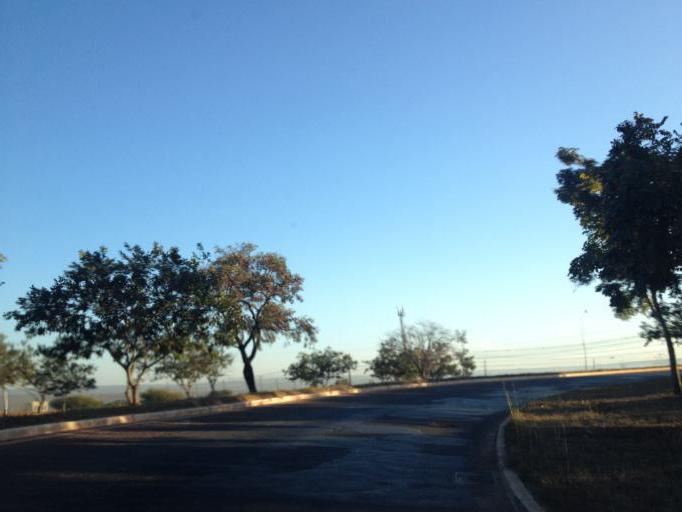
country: BR
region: Federal District
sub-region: Brasilia
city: Brasilia
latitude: -15.7568
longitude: -47.9286
